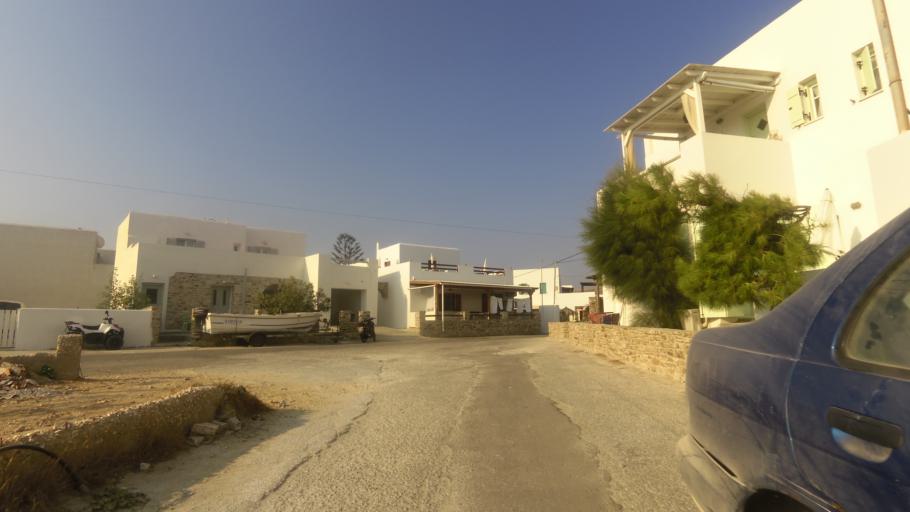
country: GR
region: South Aegean
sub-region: Nomos Kykladon
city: Antiparos
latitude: 37.0417
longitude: 25.0815
